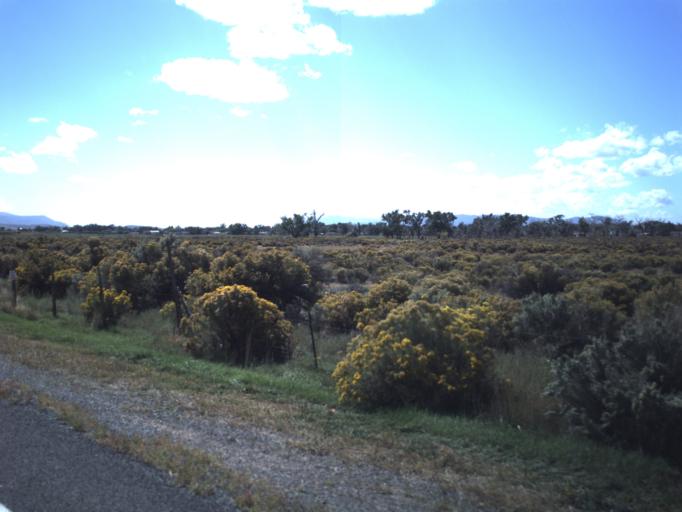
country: US
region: Utah
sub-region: Iron County
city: Enoch
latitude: 37.7607
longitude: -113.0553
